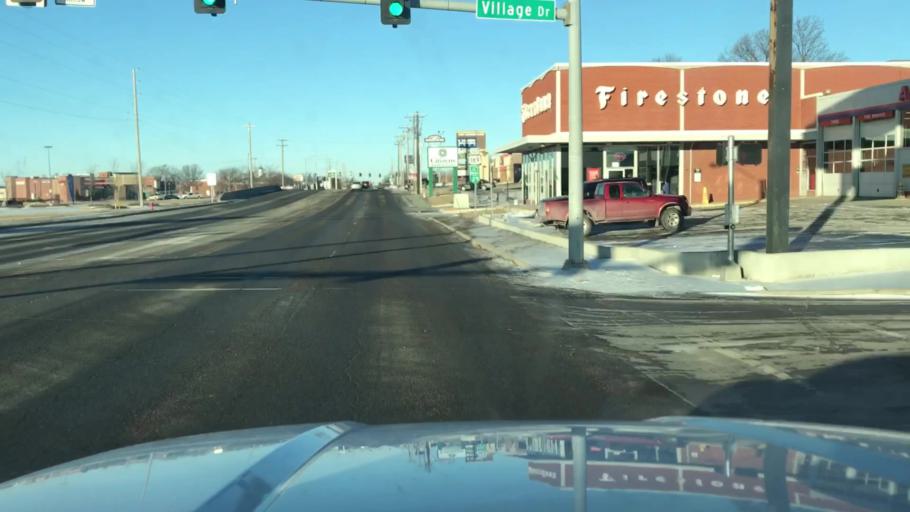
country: US
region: Missouri
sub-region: Buchanan County
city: Saint Joseph
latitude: 39.7771
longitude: -94.8000
